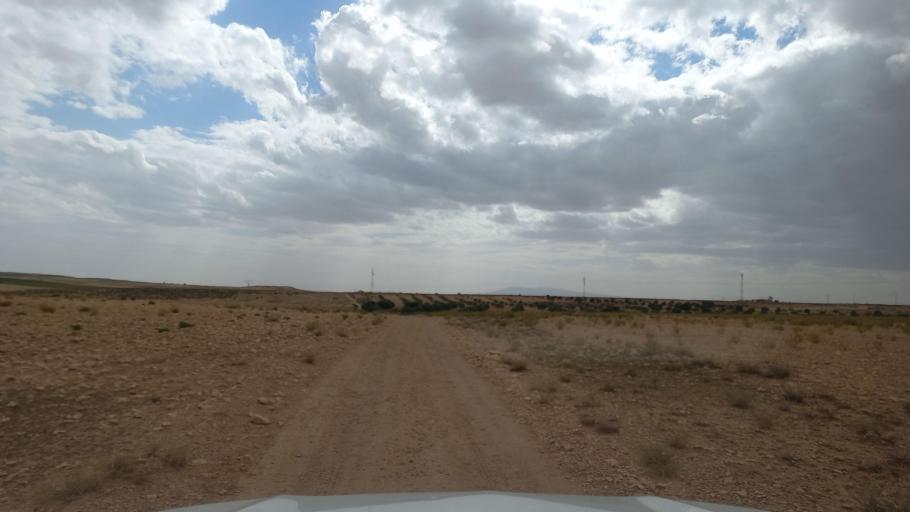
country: TN
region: Al Qasrayn
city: Sbiba
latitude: 35.3861
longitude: 9.1051
